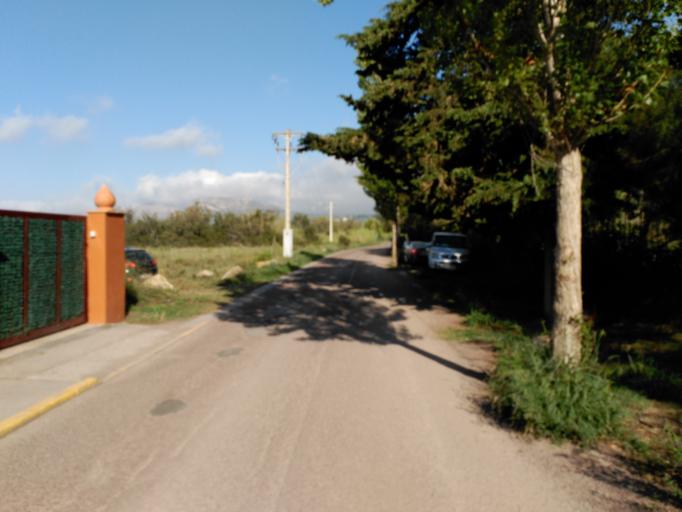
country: ES
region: Catalonia
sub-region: Provincia de Girona
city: Torroella de Montgri
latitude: 42.0446
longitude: 3.1937
